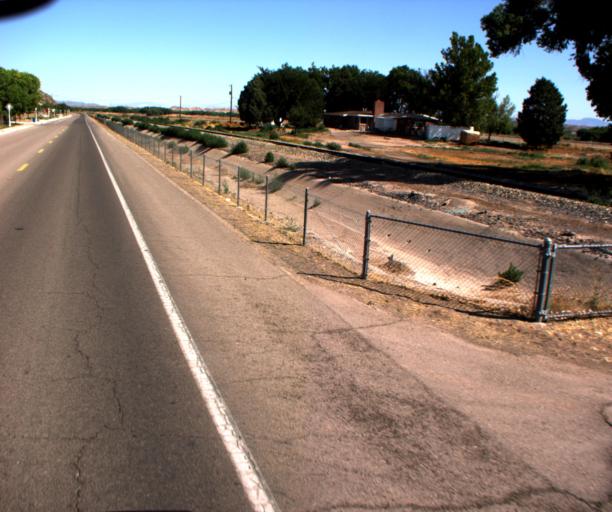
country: US
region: Arizona
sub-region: Greenlee County
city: Clifton
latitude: 32.7257
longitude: -109.1081
